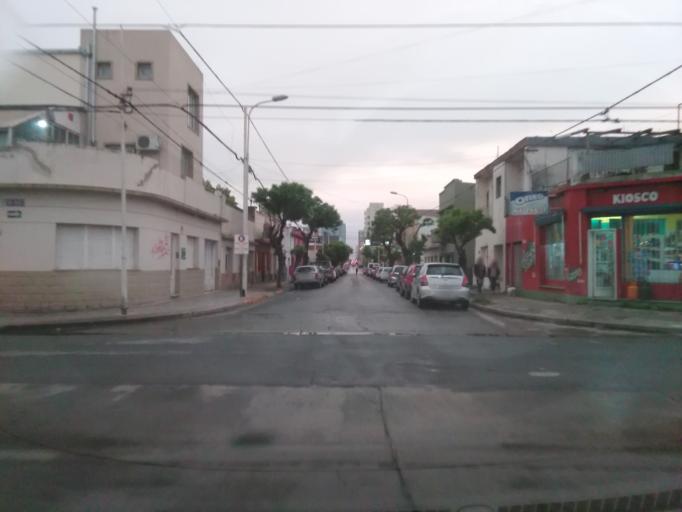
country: AR
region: Buenos Aires
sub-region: Partido de Tandil
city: Tandil
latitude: -37.3272
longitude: -59.1429
